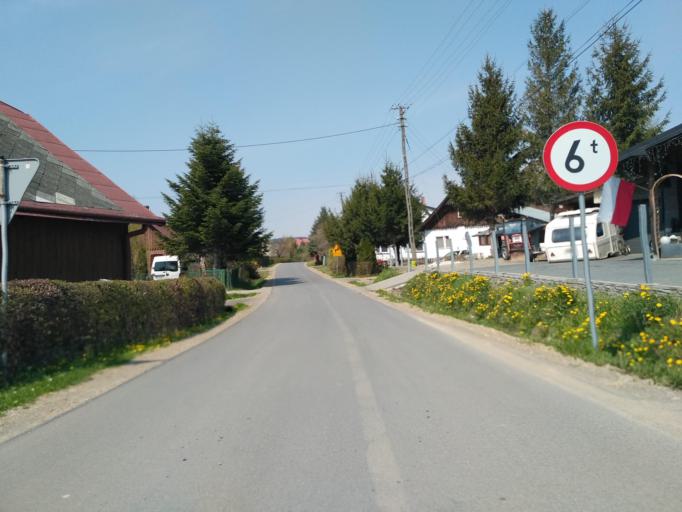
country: PL
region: Subcarpathian Voivodeship
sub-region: Powiat krosnienski
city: Chorkowka
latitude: 49.6329
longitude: 21.6990
